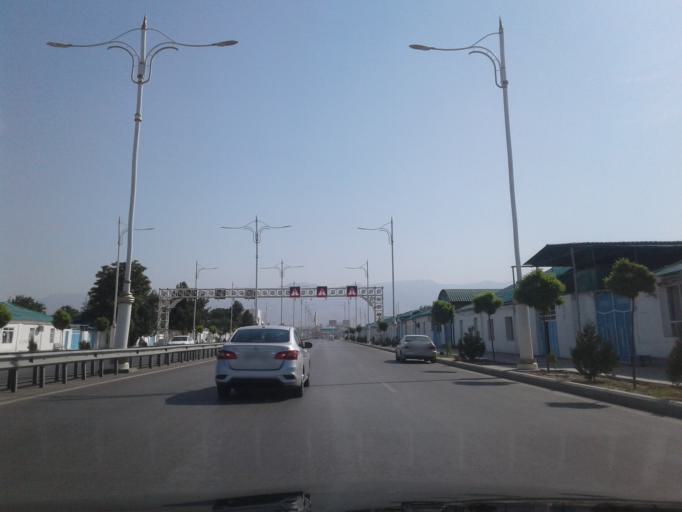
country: TM
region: Ahal
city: Ashgabat
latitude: 37.9527
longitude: 58.4118
